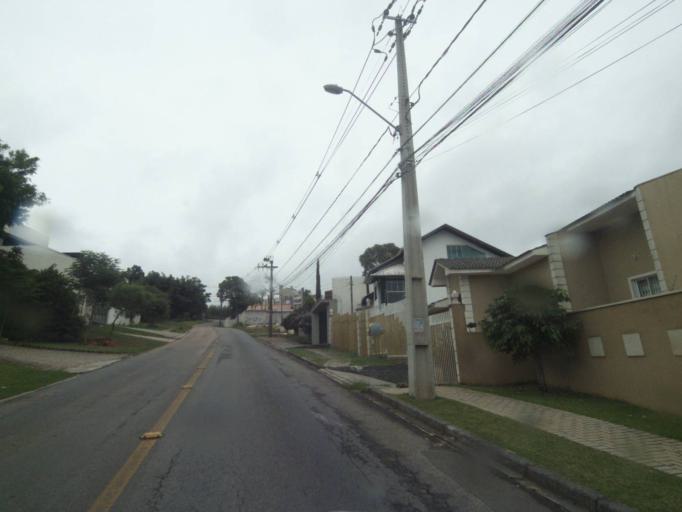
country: BR
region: Parana
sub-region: Curitiba
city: Curitiba
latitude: -25.4240
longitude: -49.3251
